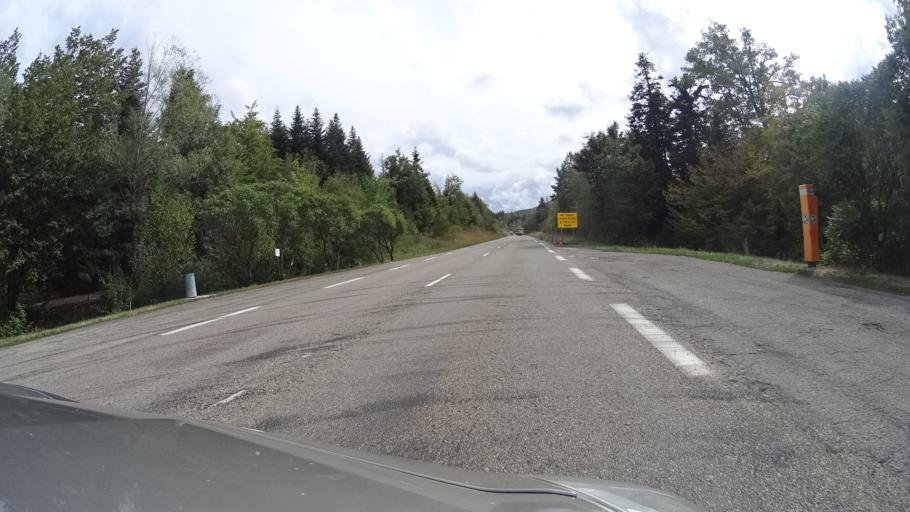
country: FR
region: Franche-Comte
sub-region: Departement du Jura
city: Champagnole
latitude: 46.7369
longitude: 5.9285
